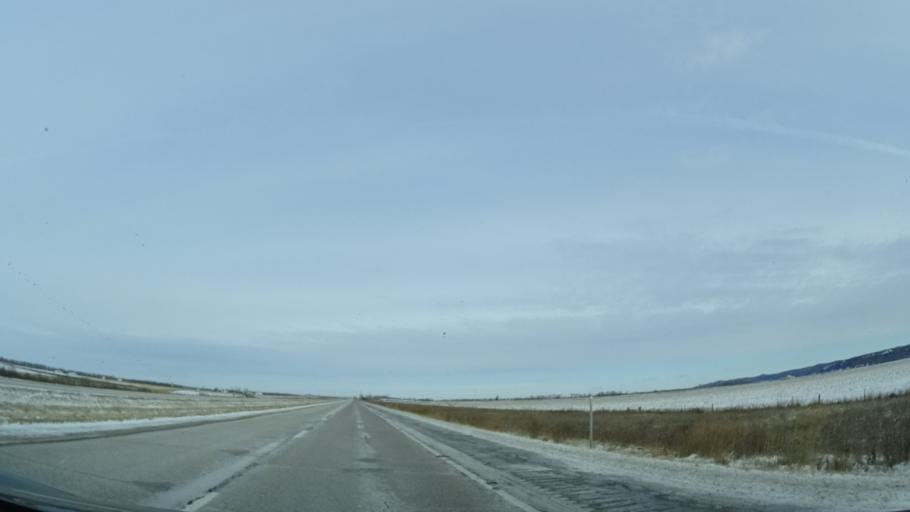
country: US
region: Nebraska
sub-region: Burt County
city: Tekamah
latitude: 41.7638
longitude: -96.0463
